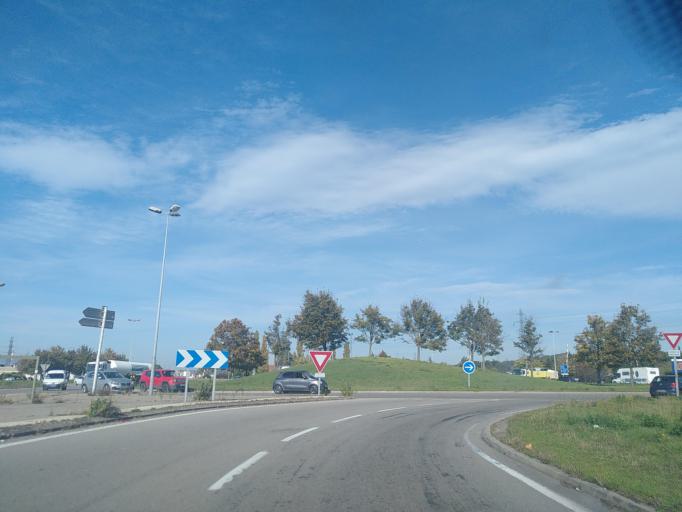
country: FR
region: Rhone-Alpes
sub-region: Departement de l'Isere
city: Chanas
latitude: 45.3172
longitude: 4.8084
